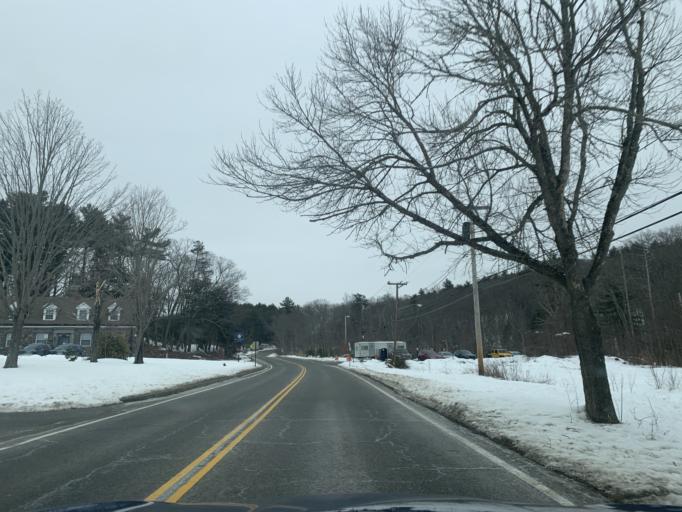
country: US
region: Massachusetts
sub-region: Norfolk County
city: Milton
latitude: 42.2140
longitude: -71.0933
